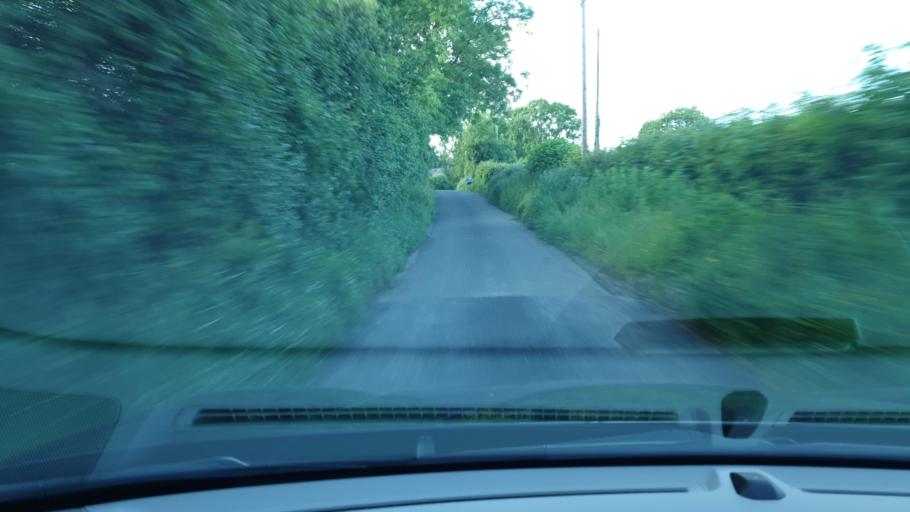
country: IE
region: Leinster
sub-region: An Mhi
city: Ashbourne
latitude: 53.5142
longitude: -6.3849
